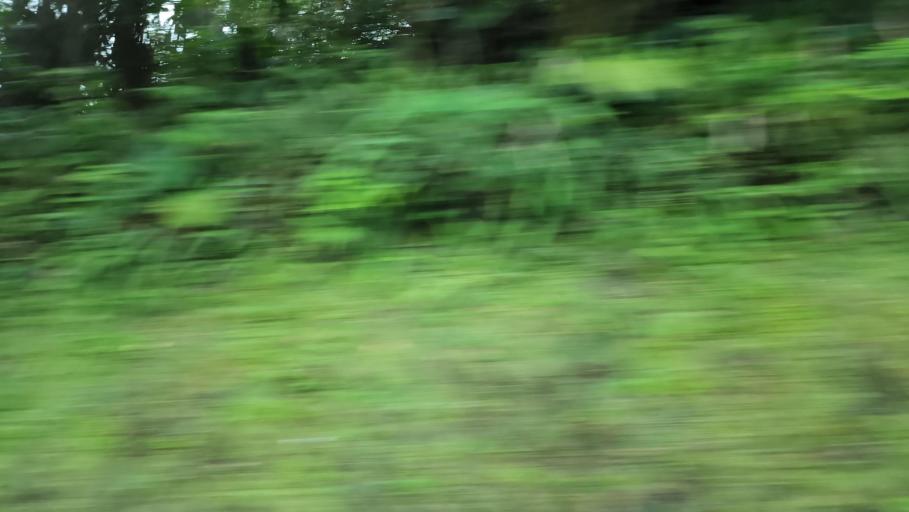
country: TW
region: Taipei
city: Taipei
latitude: 25.1454
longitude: 121.6045
